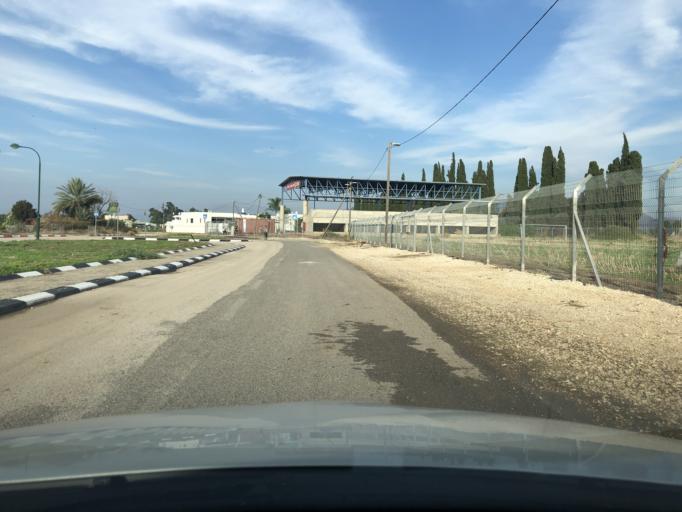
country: IL
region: Northern District
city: Yavne'el
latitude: 32.6587
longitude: 35.5850
